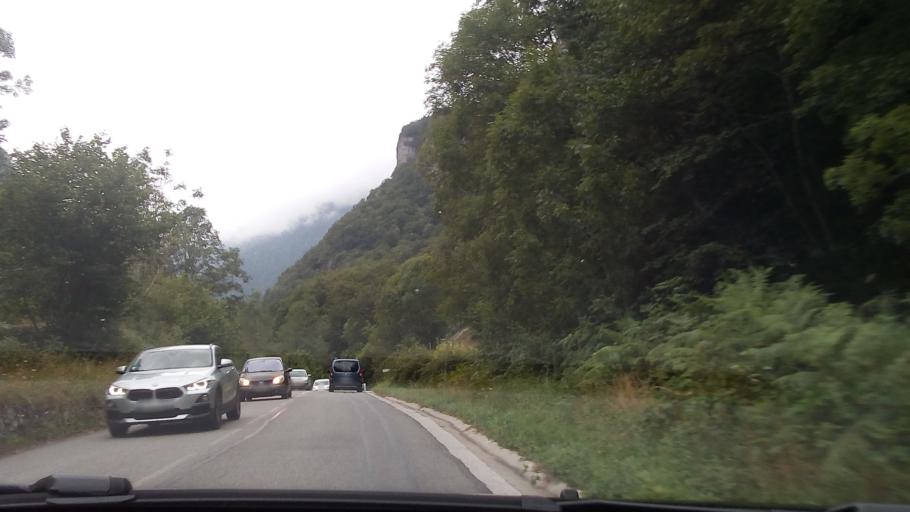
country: FR
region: Aquitaine
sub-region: Departement des Pyrenees-Atlantiques
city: Laruns
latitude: 42.9453
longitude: -0.4423
